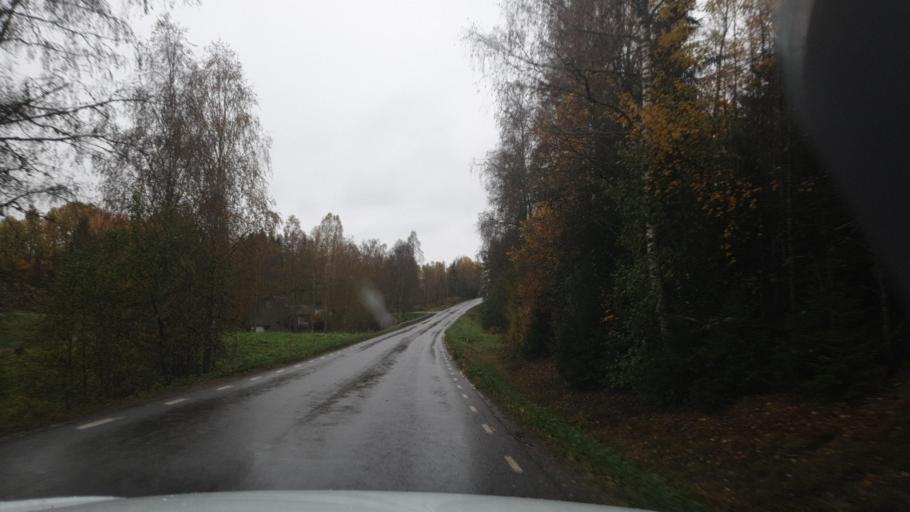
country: SE
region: Vaermland
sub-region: Eda Kommun
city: Charlottenberg
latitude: 59.8013
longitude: 12.1540
